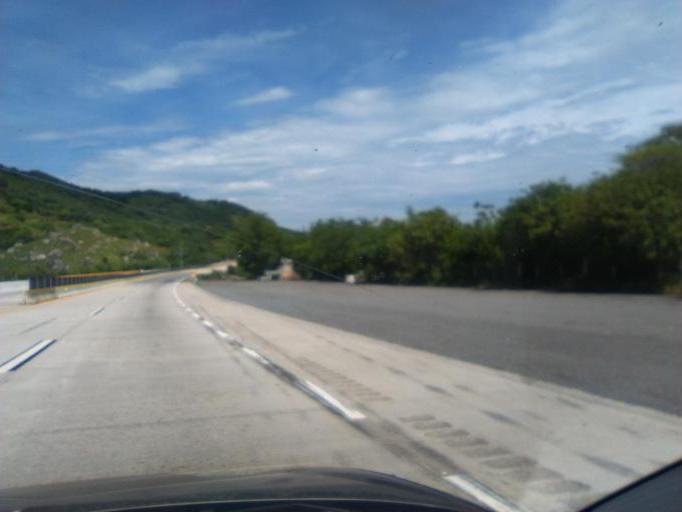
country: MX
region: Guerrero
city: Xaltianguis
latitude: 17.0201
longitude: -99.6562
